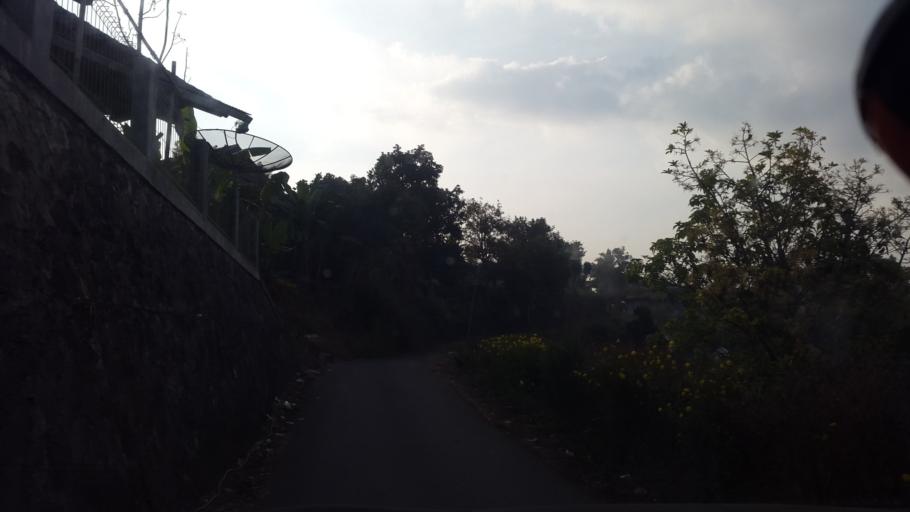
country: ID
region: West Java
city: Sukabumi
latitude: -6.8403
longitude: 106.8920
